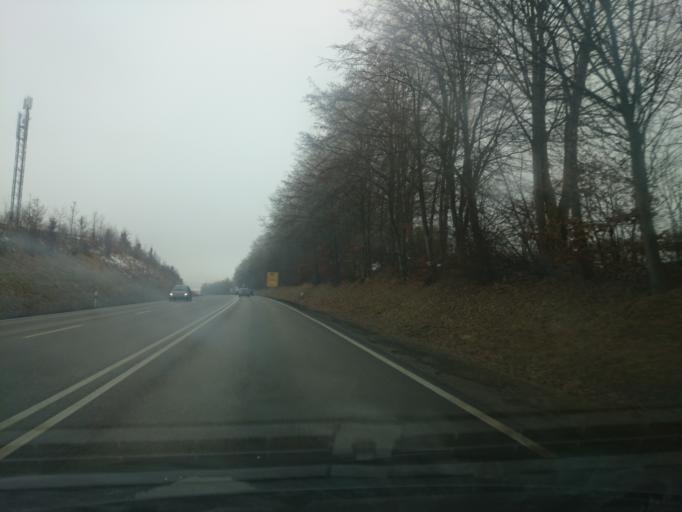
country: DE
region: Bavaria
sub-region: Swabia
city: Aichach
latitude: 48.4497
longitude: 11.1436
